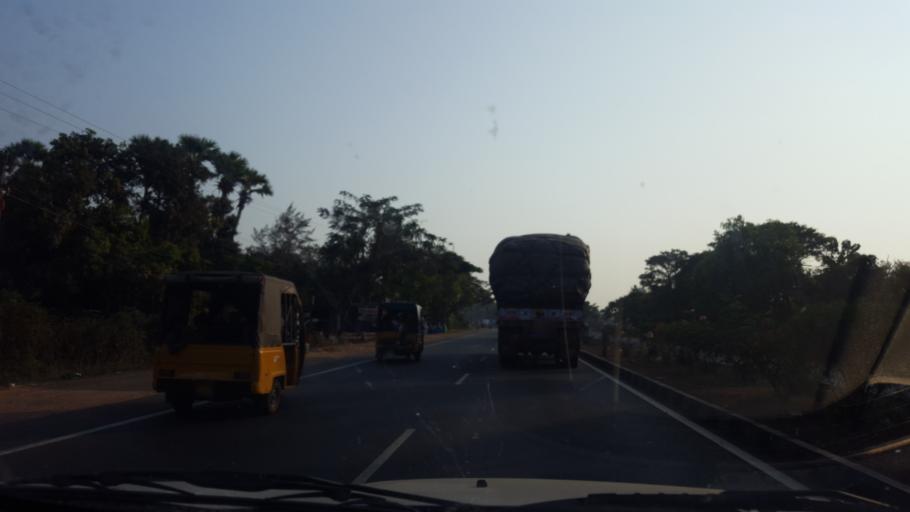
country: IN
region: Andhra Pradesh
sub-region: East Godavari
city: Pithapuram
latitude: 17.2553
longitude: 82.3720
